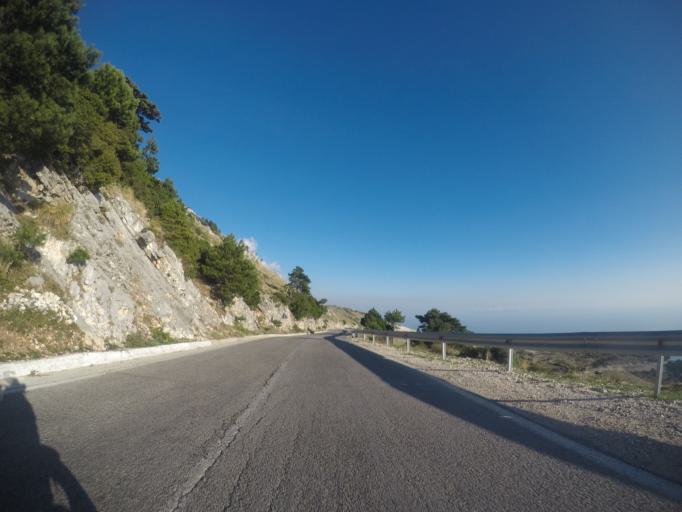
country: AL
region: Vlore
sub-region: Rrethi i Vlores
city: Vranisht
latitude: 40.1954
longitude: 19.5991
